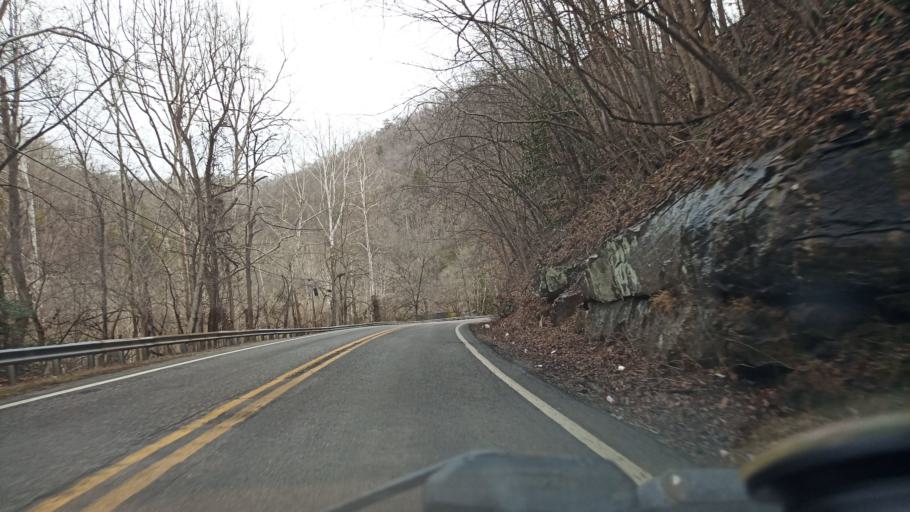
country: US
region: West Virginia
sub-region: Logan County
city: Mallory
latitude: 37.6537
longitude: -81.8527
